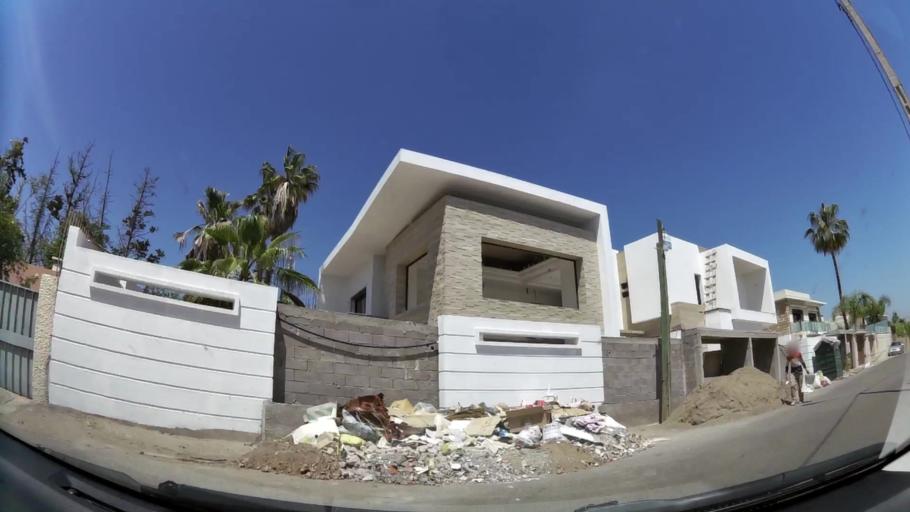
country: MA
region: Souss-Massa-Draa
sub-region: Agadir-Ida-ou-Tnan
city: Agadir
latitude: 30.4304
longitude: -9.5986
